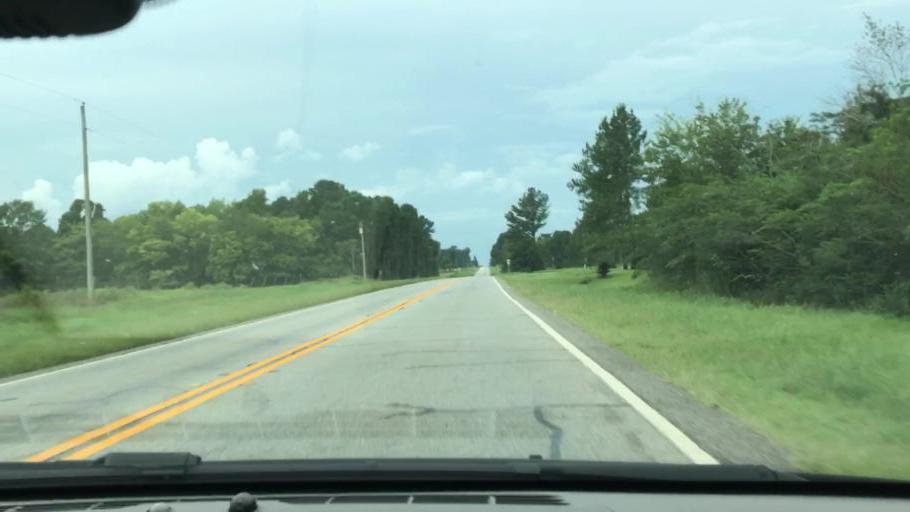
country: US
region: Georgia
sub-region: Early County
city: Blakely
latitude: 31.3303
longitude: -85.0001
